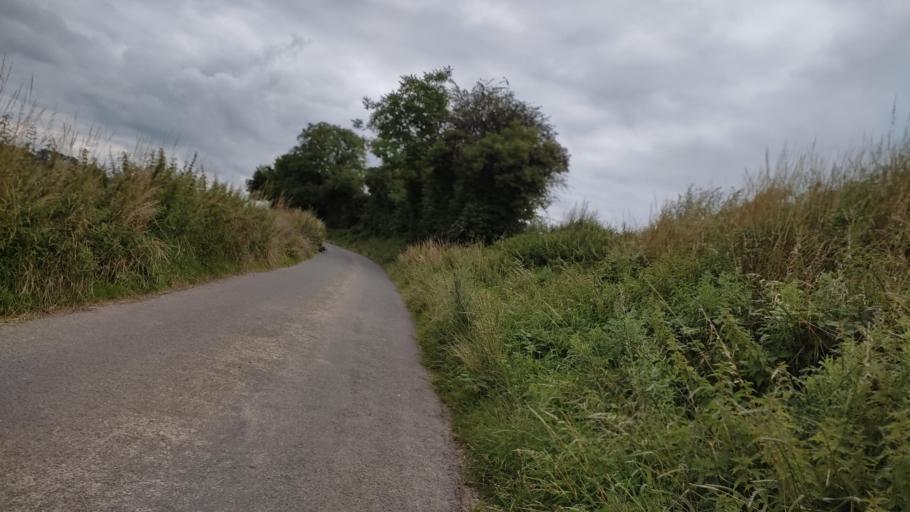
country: FR
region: Nord-Pas-de-Calais
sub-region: Departement du Pas-de-Calais
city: Beaumetz-les-Loges
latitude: 50.2497
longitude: 2.6394
